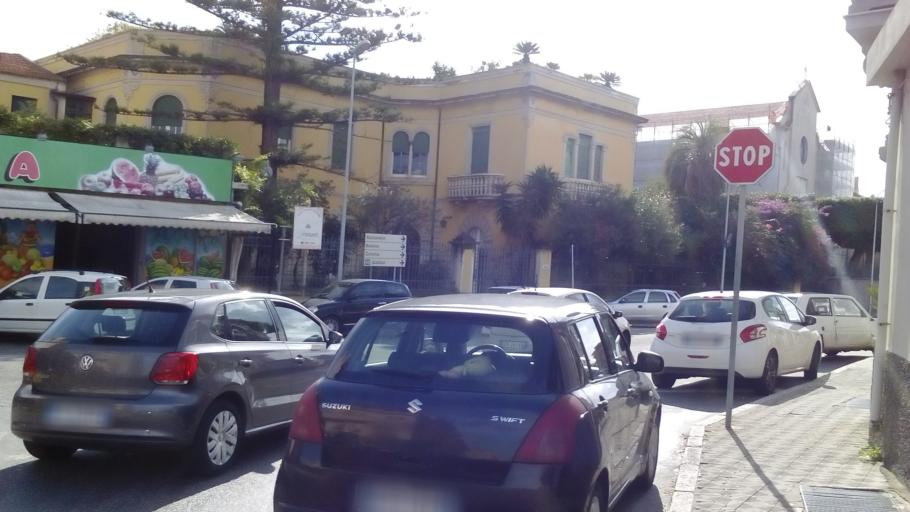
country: IT
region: Calabria
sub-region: Provincia di Reggio Calabria
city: Campo Calabro
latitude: 38.2124
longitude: 15.6371
